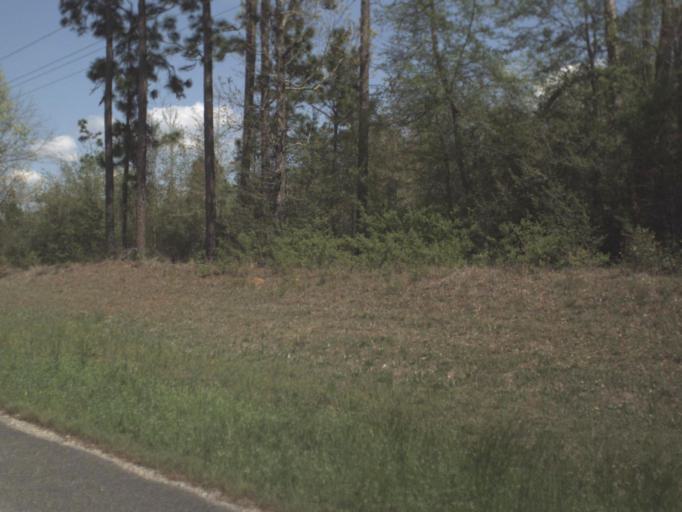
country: US
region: Alabama
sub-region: Escambia County
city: East Brewton
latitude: 30.9464
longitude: -87.0720
